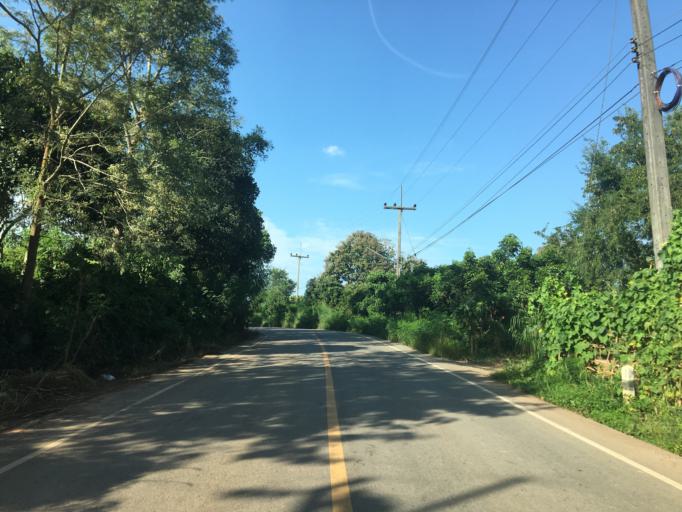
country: TH
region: Chiang Rai
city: Pa Daet
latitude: 19.4286
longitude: 100.0146
